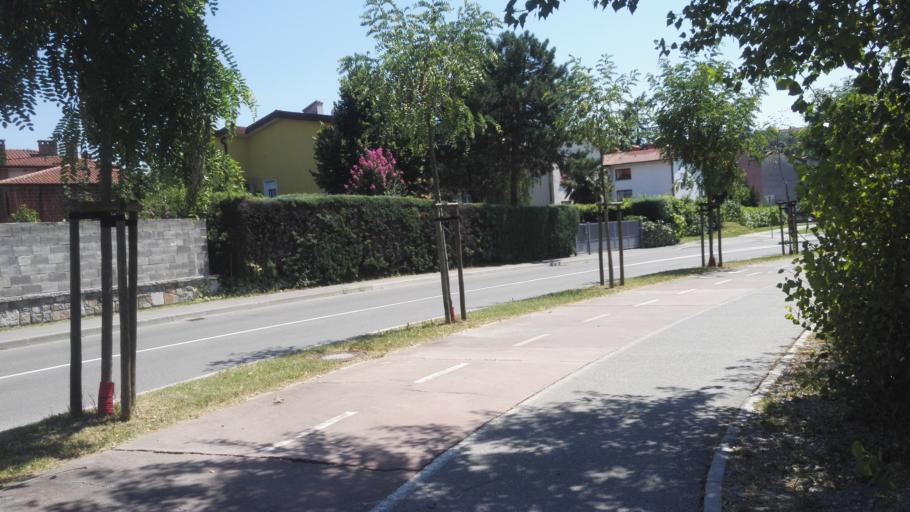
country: SI
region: Nova Gorica
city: Nova Gorica
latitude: 45.9563
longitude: 13.6384
